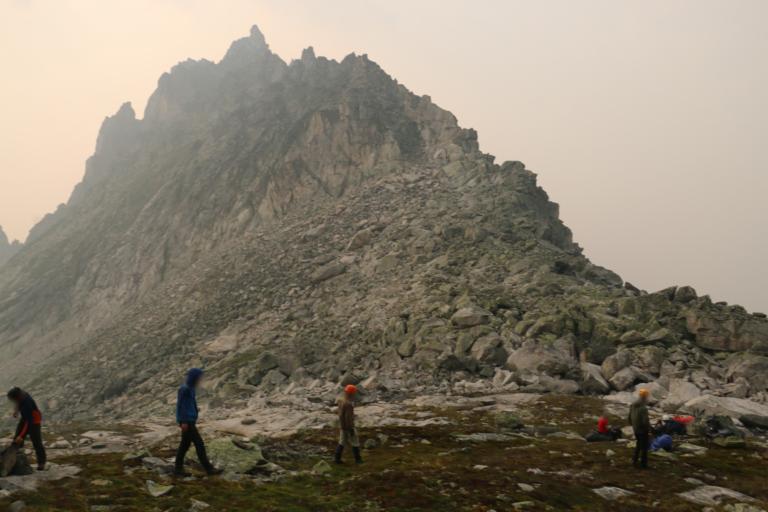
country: RU
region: Respublika Buryatiya
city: Kichera
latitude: 56.2288
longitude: 110.8659
